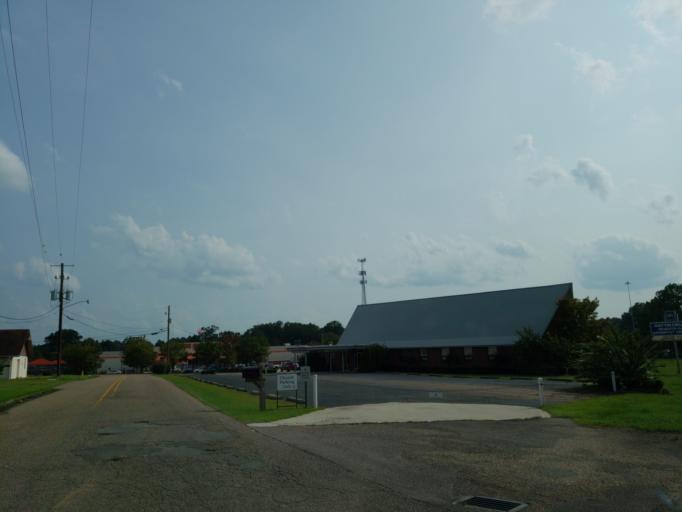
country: US
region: Mississippi
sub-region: Lamar County
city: West Hattiesburg
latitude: 31.3240
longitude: -89.3501
